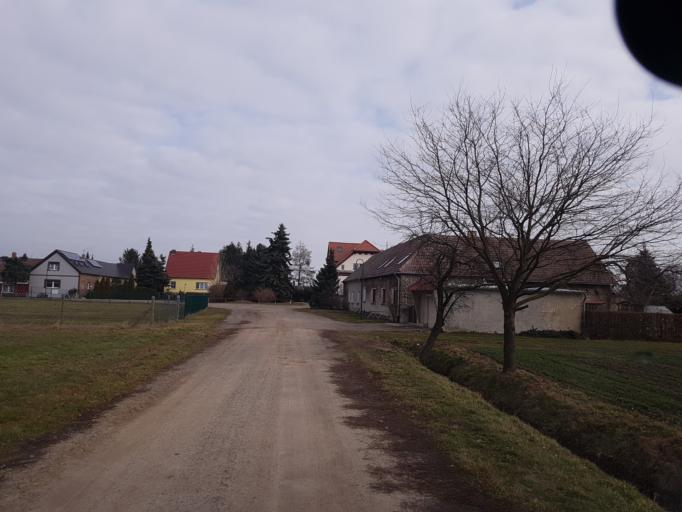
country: DE
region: Brandenburg
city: Doberlug-Kirchhain
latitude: 51.6877
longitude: 13.5141
